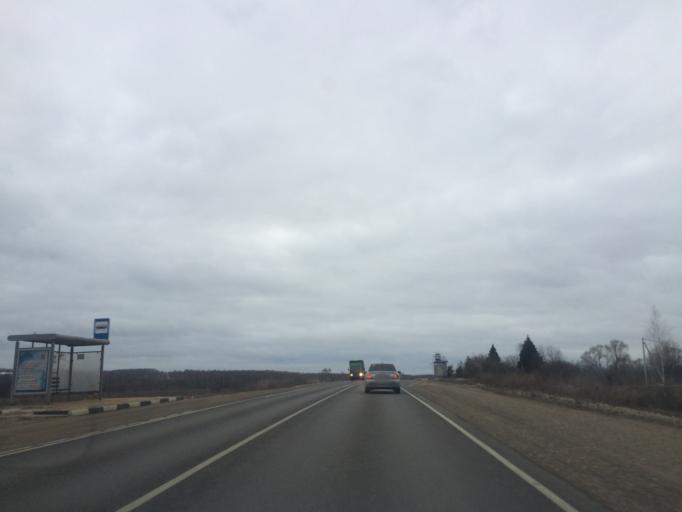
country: RU
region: Tula
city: Krapivna
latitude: 54.1166
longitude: 37.2228
